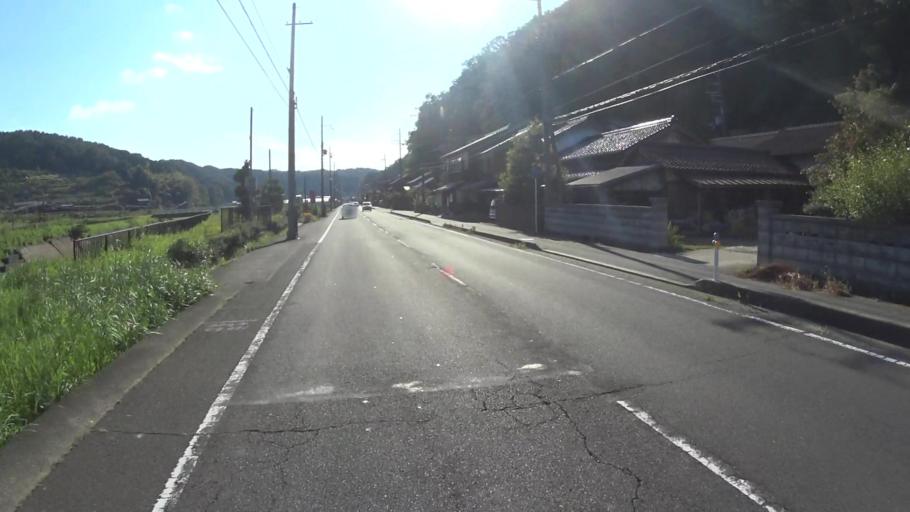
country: JP
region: Hyogo
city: Toyooka
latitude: 35.6543
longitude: 134.9828
